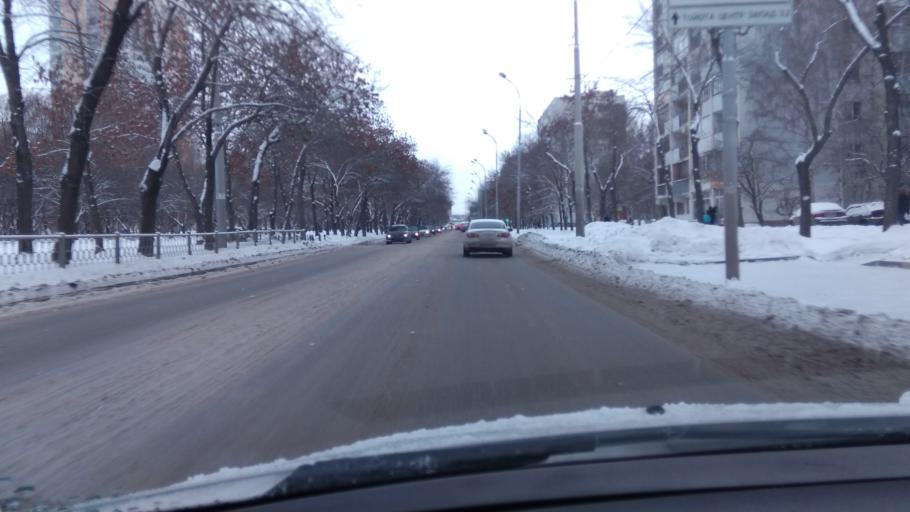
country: RU
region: Sverdlovsk
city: Sovkhoznyy
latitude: 56.8151
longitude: 60.5690
